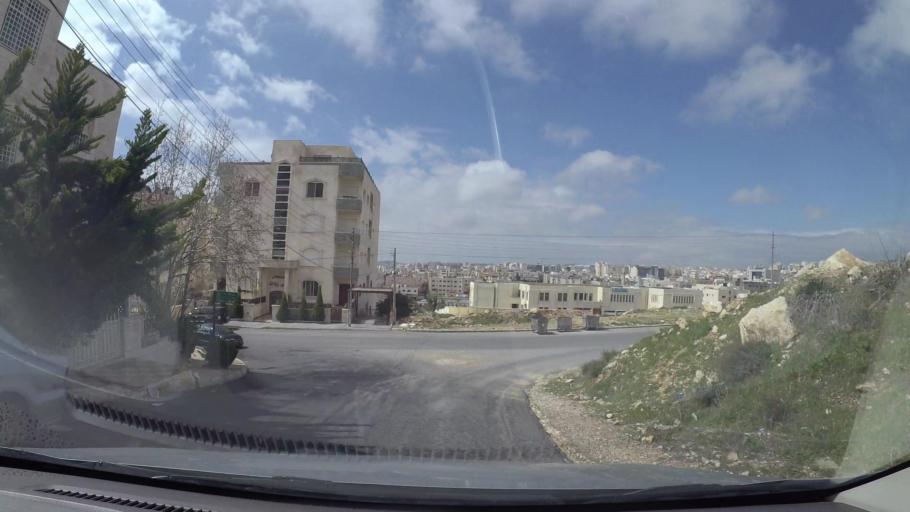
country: JO
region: Amman
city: Al Jubayhah
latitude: 31.9943
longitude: 35.8510
